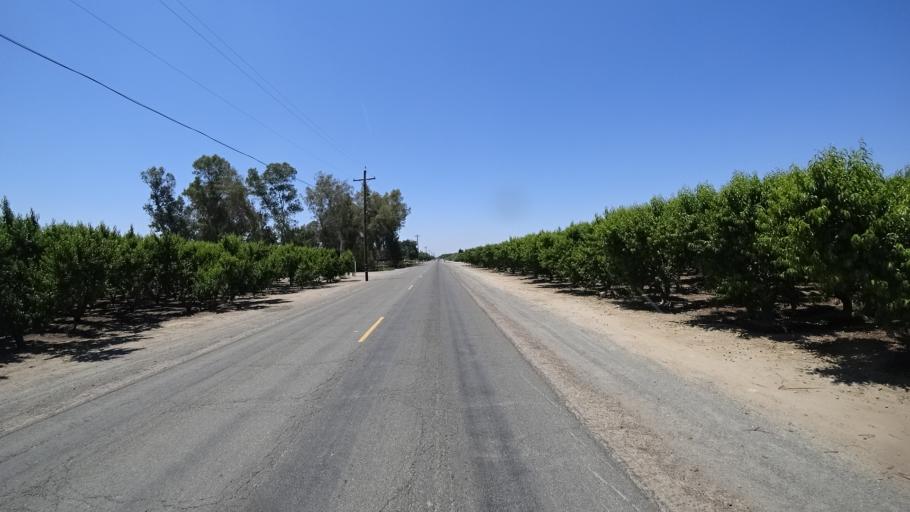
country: US
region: California
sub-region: Fresno County
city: Kingsburg
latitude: 36.4305
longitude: -119.5529
